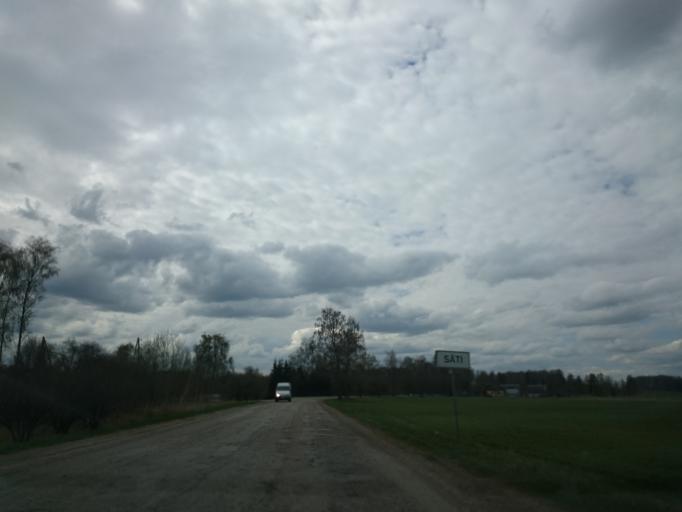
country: LV
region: Jaunpils
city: Jaunpils
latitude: 56.9107
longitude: 22.9765
